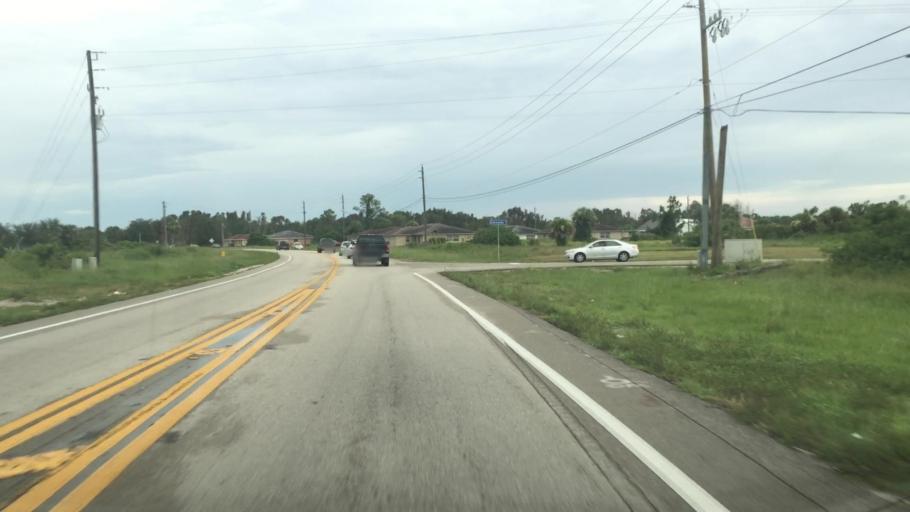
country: US
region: Florida
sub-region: Lee County
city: Gateway
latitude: 26.6133
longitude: -81.7484
